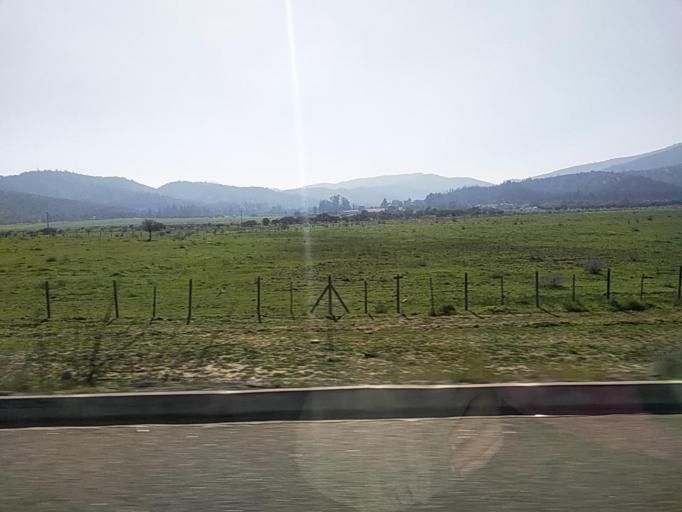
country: CL
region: Valparaiso
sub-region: San Antonio Province
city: El Tabo
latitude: -33.3907
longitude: -71.4432
